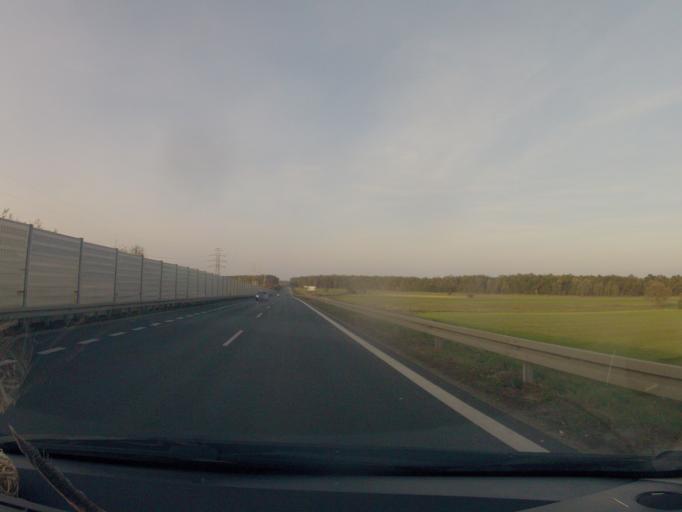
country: PL
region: Opole Voivodeship
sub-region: Powiat opolski
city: Opole
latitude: 50.6584
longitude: 17.9957
